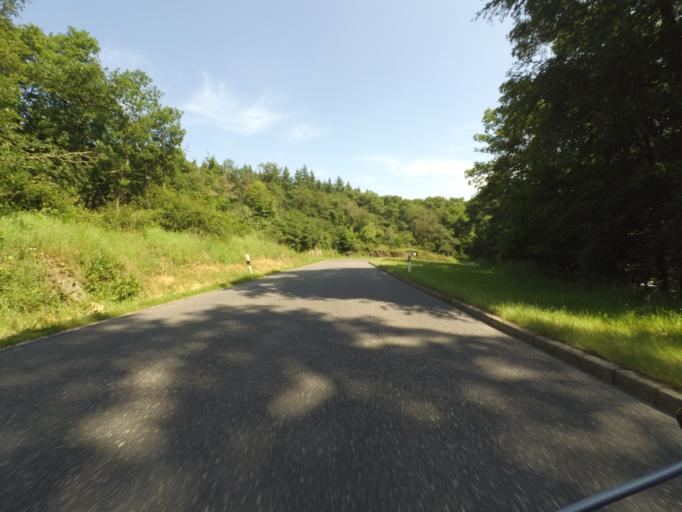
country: DE
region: Rheinland-Pfalz
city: Filsen
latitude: 50.2229
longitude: 7.5585
